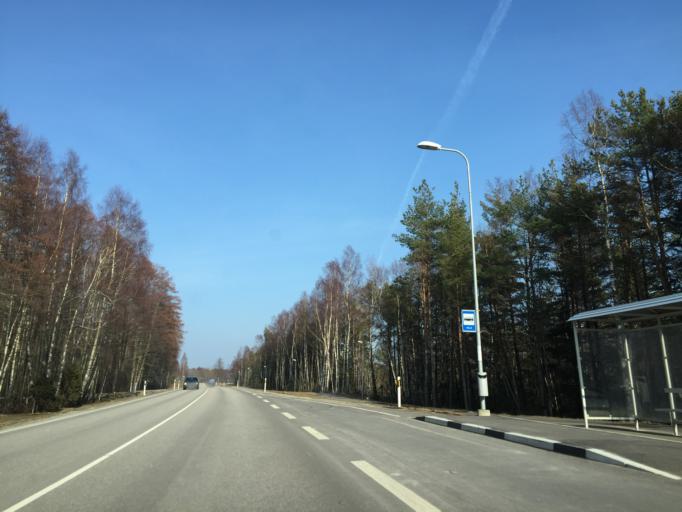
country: EE
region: Saare
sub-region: Kuressaare linn
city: Kuressaare
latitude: 58.2228
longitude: 22.3603
